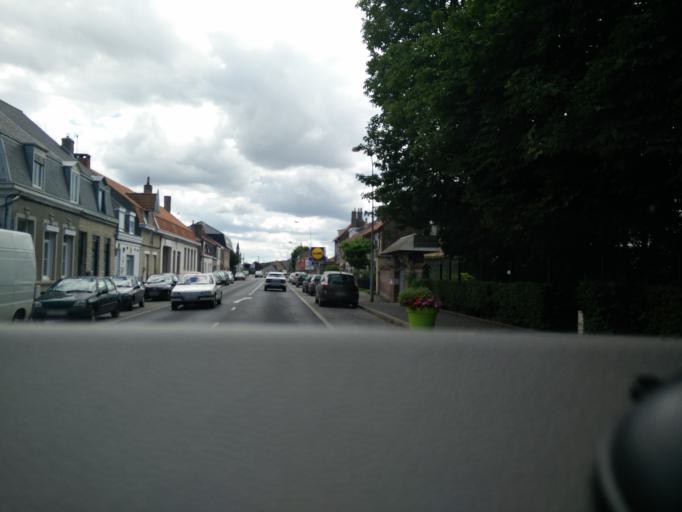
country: FR
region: Nord-Pas-de-Calais
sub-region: Departement du Nord
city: Bergues
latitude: 50.9600
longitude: 2.4334
